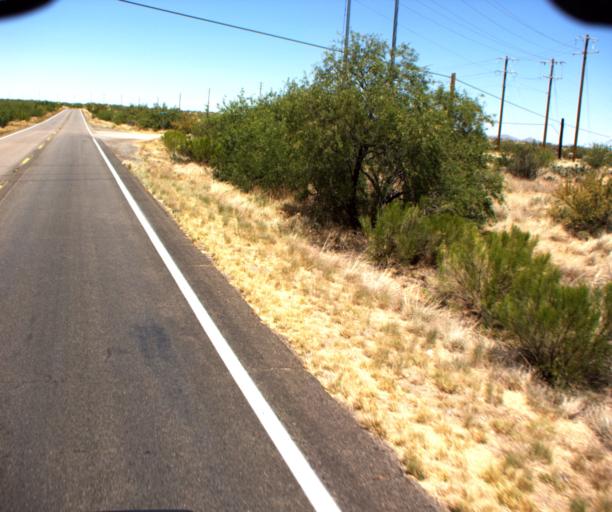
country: US
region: Arizona
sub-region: Pima County
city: Catalina
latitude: 32.5740
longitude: -110.9474
